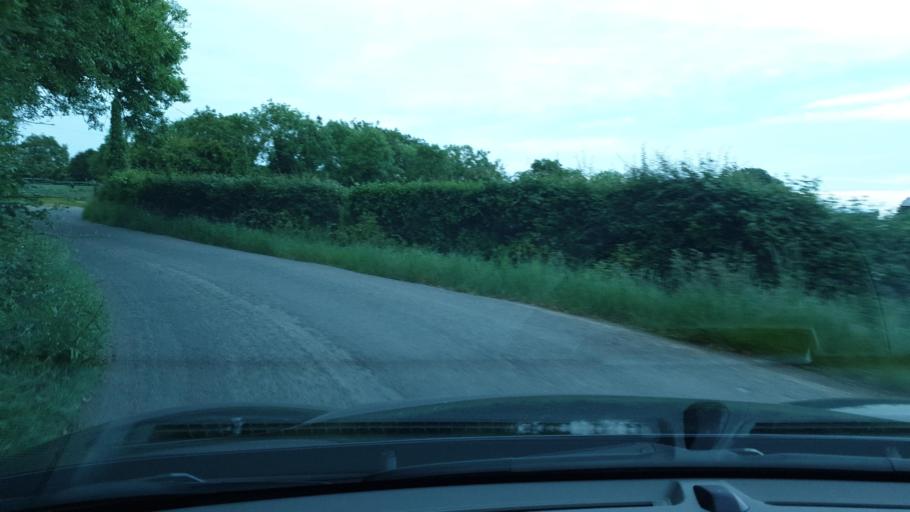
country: IE
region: Leinster
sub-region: An Mhi
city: Ashbourne
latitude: 53.5235
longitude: -6.3834
